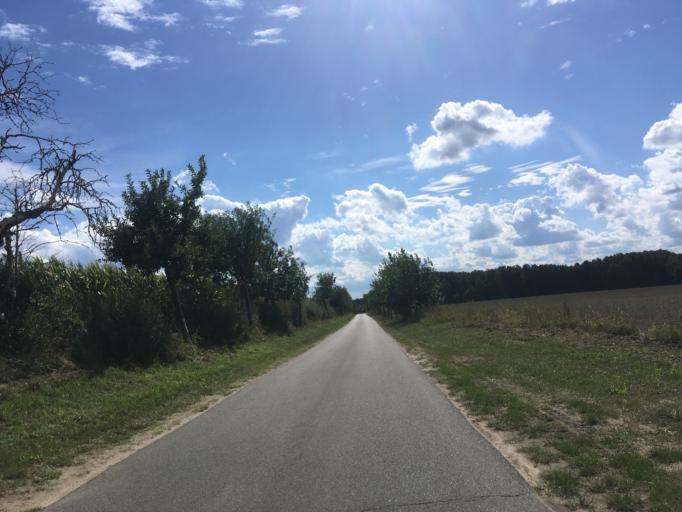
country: DE
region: Brandenburg
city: Angermunde
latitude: 52.9831
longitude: 13.9953
